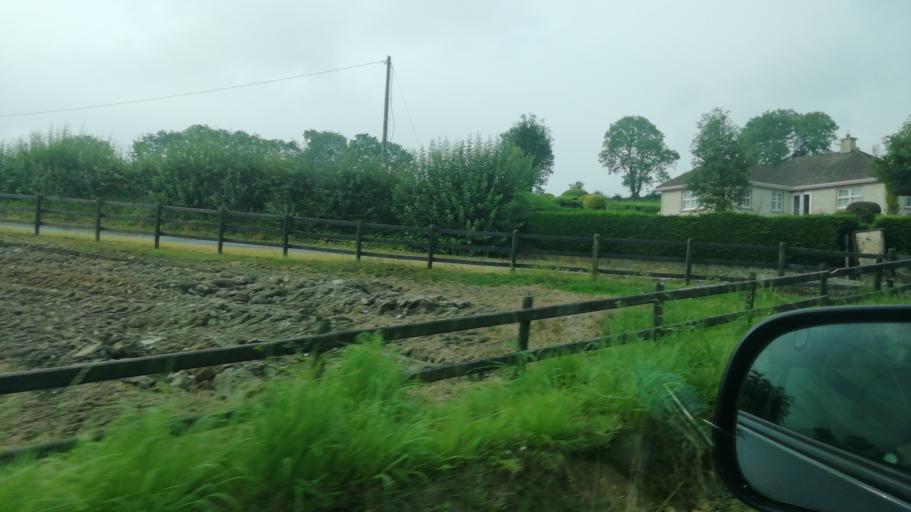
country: IE
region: Munster
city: Fethard
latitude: 52.5827
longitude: -7.6108
